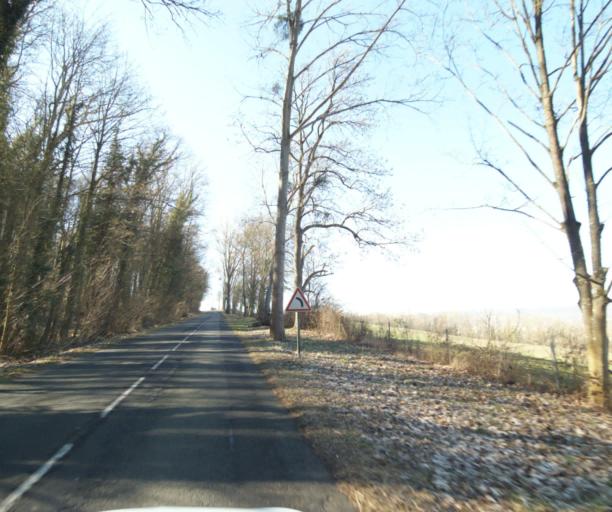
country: FR
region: Lorraine
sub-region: Departement de Meurthe-et-Moselle
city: Lay-Saint-Christophe
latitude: 48.7372
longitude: 6.1870
